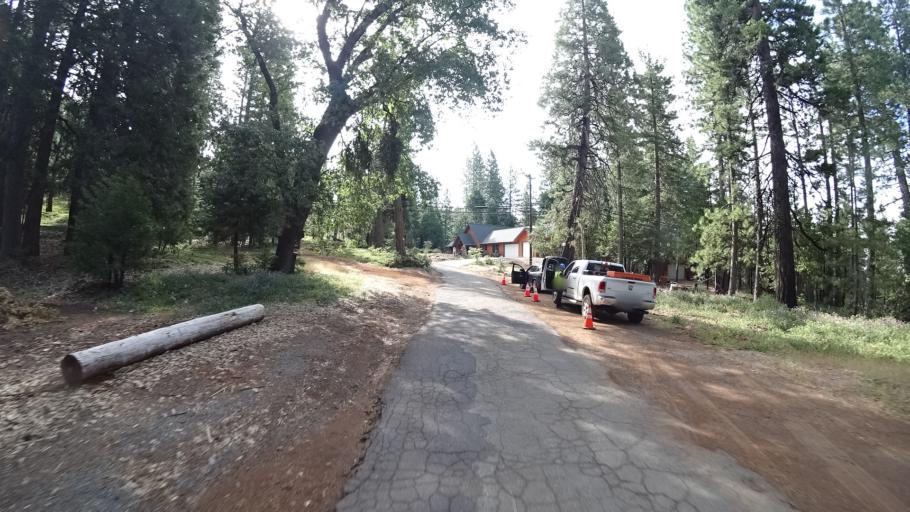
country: US
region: California
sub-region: Calaveras County
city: Arnold
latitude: 38.2678
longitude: -120.3305
